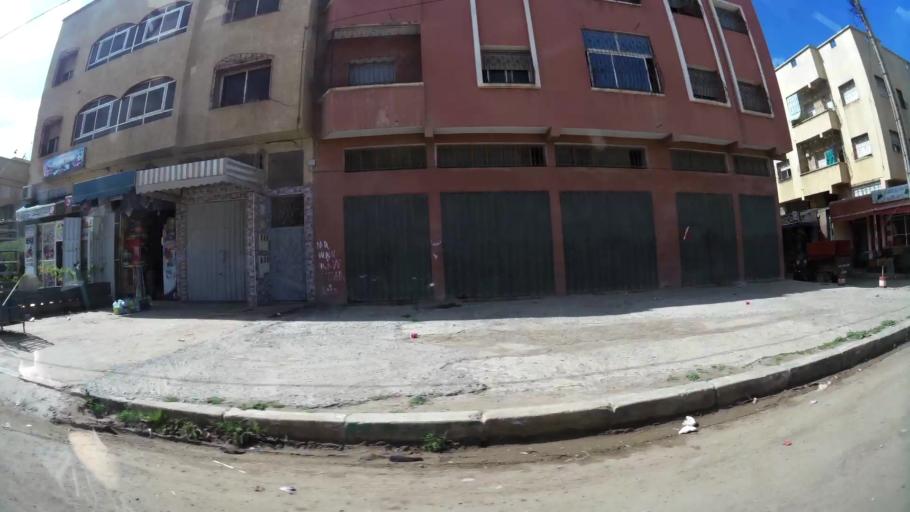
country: MA
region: Grand Casablanca
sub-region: Mediouna
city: Mediouna
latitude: 33.4566
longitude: -7.5116
